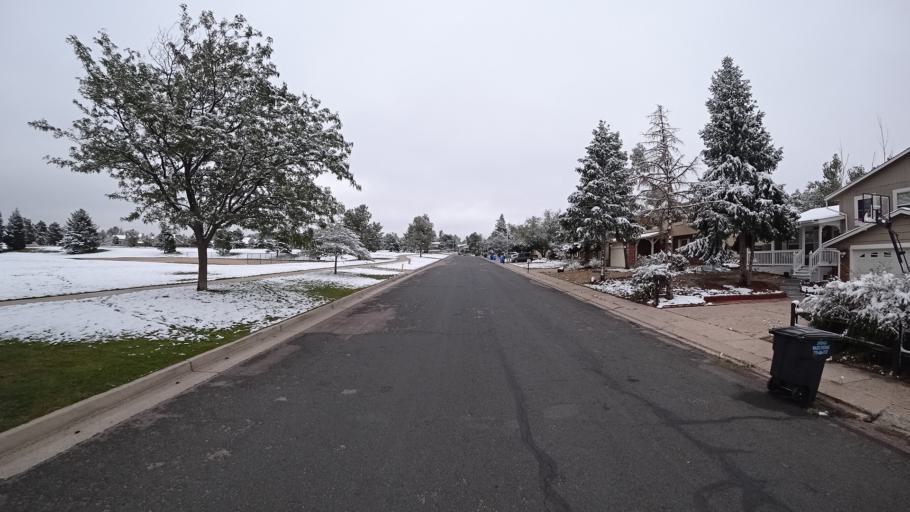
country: US
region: Colorado
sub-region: El Paso County
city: Colorado Springs
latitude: 38.9241
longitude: -104.7854
